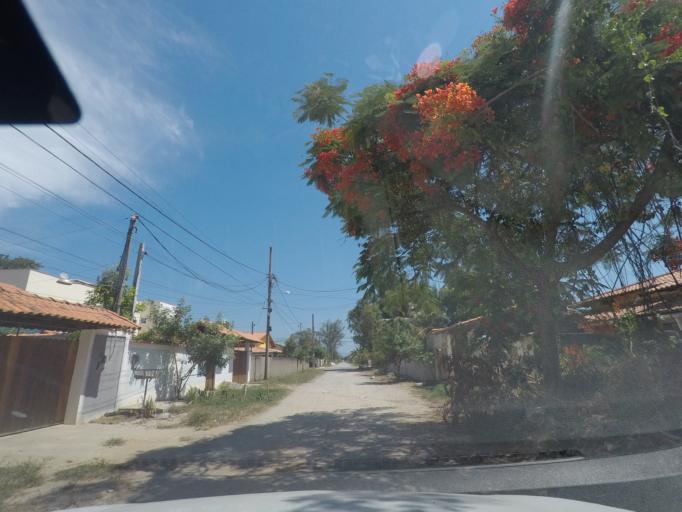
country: BR
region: Rio de Janeiro
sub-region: Marica
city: Marica
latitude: -22.9560
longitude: -42.9595
